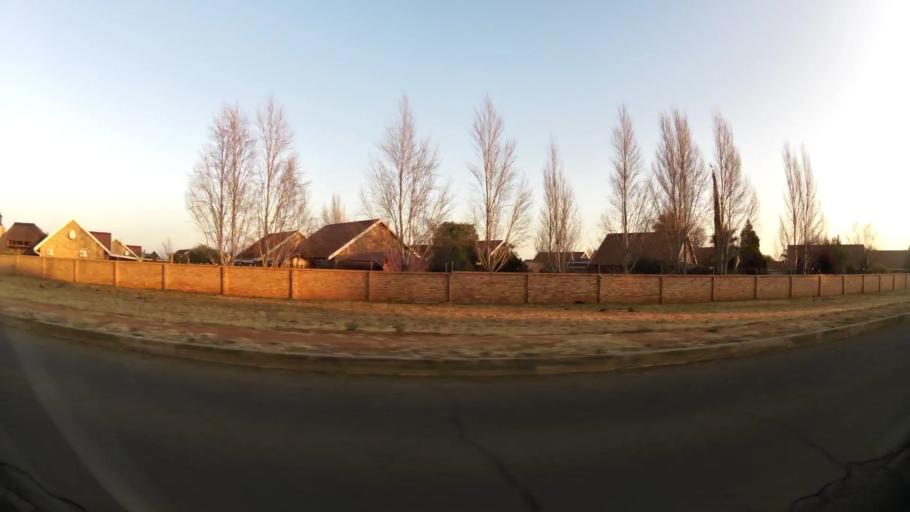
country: ZA
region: Orange Free State
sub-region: Mangaung Metropolitan Municipality
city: Bloemfontein
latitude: -29.0926
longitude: 26.1500
